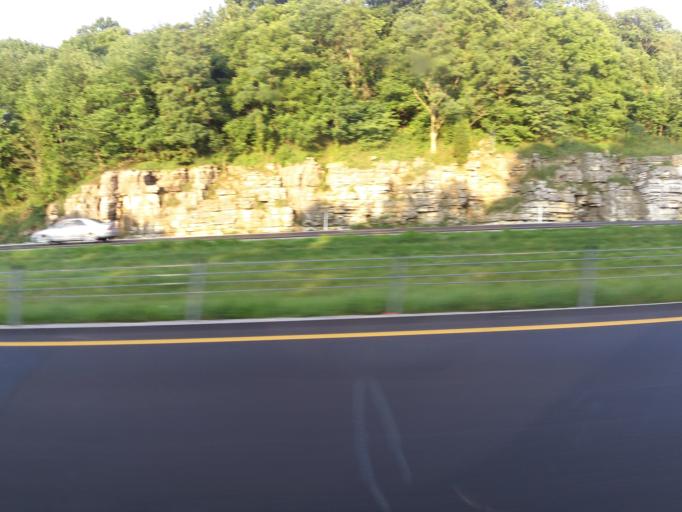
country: US
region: Kentucky
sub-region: Rockcastle County
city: Brodhead
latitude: 37.4301
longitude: -84.3437
